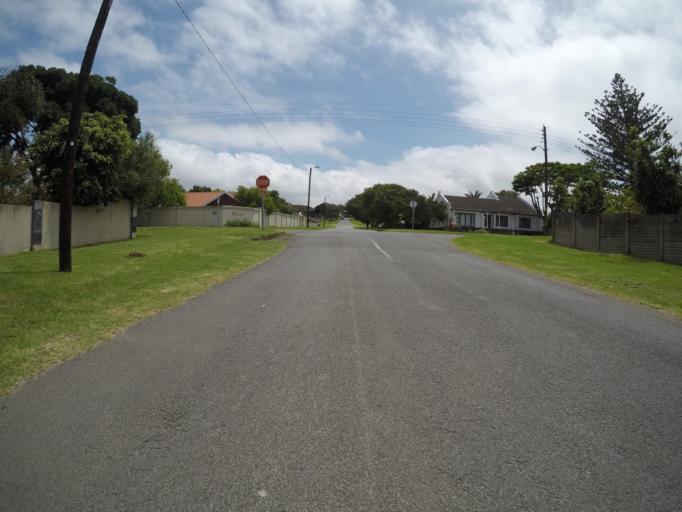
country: ZA
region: Eastern Cape
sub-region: Buffalo City Metropolitan Municipality
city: East London
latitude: -32.9429
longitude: 28.0080
